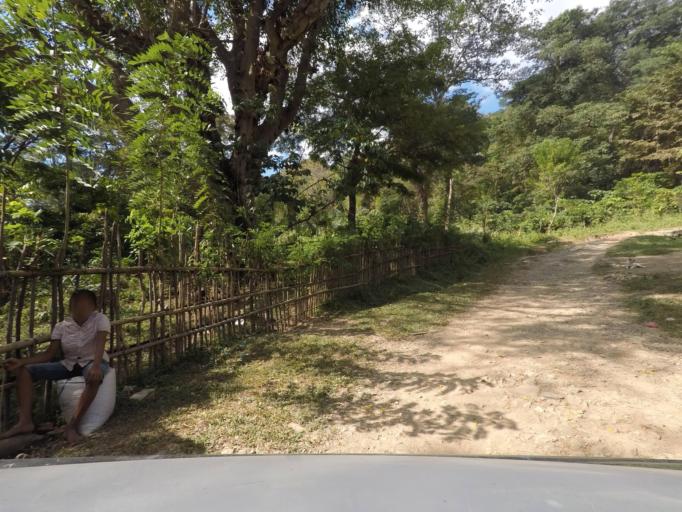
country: TL
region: Ermera
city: Gleno
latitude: -8.7182
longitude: 125.3065
